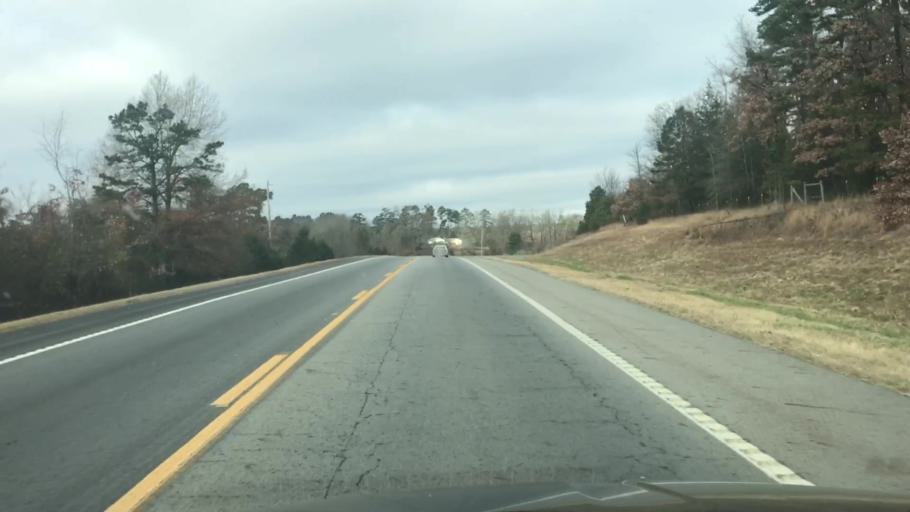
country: US
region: Arkansas
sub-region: Scott County
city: Waldron
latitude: 34.8391
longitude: -94.0507
